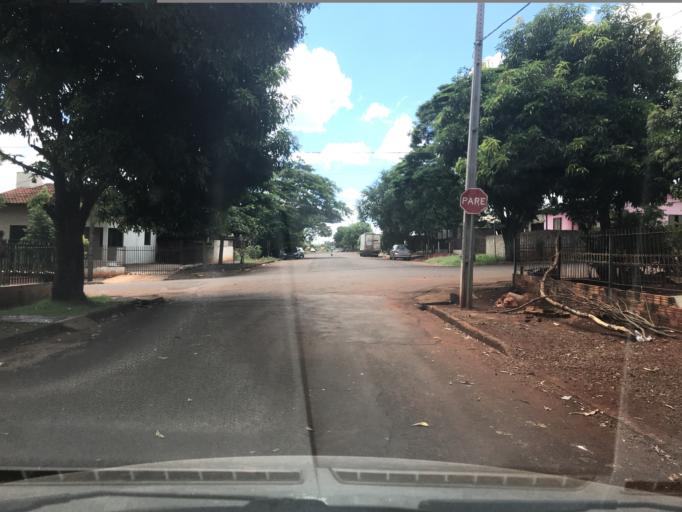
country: BR
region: Parana
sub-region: Palotina
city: Palotina
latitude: -24.2706
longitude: -53.8475
